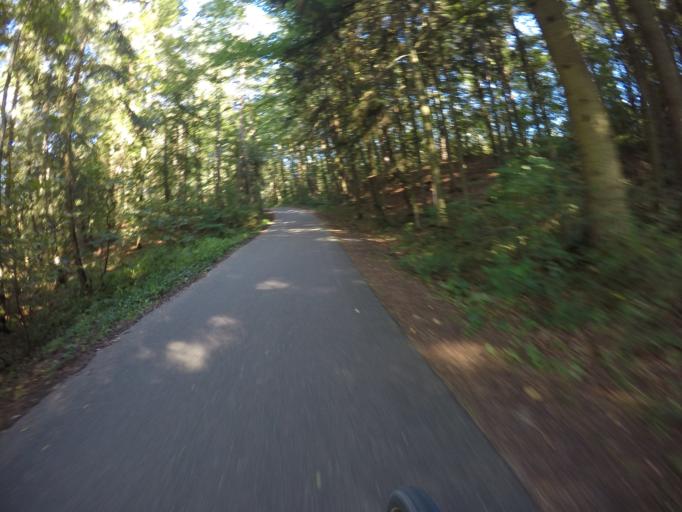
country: DE
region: Baden-Wuerttemberg
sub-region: Regierungsbezirk Stuttgart
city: Nufringen
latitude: 48.6053
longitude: 8.8916
